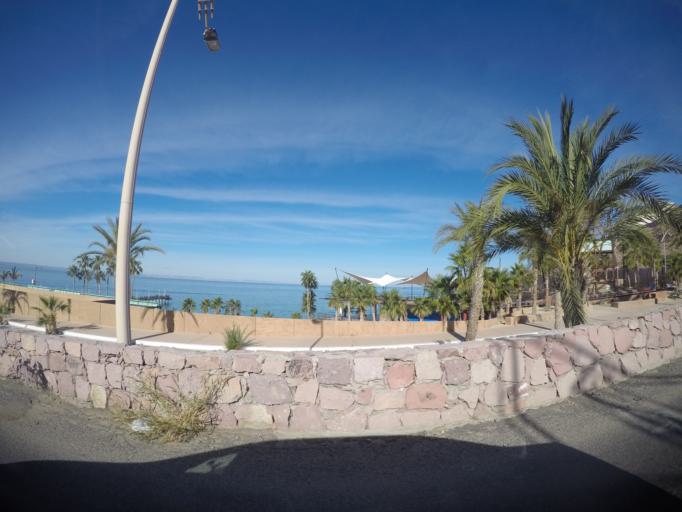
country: MX
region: Baja California Sur
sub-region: La Paz
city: La Paz
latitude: 24.1906
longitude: -110.2948
